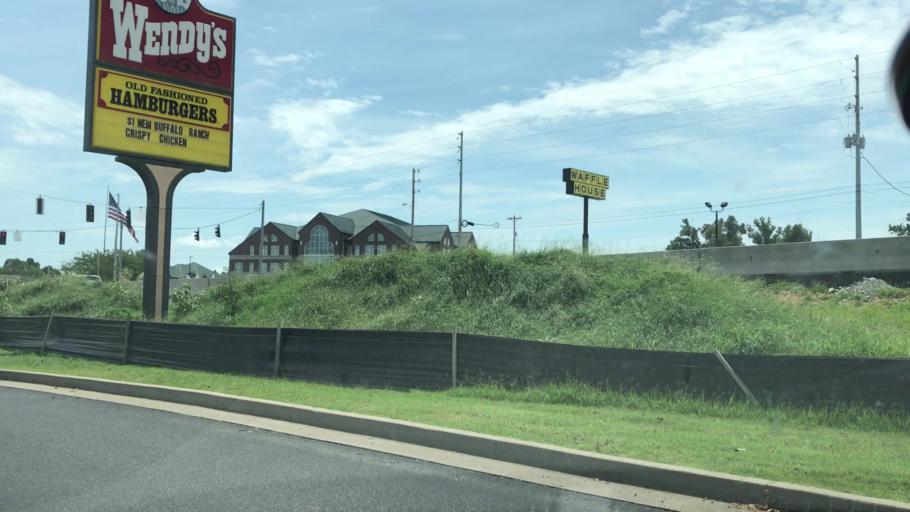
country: US
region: Kentucky
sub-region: Marshall County
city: Benton
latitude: 36.8676
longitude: -88.3609
